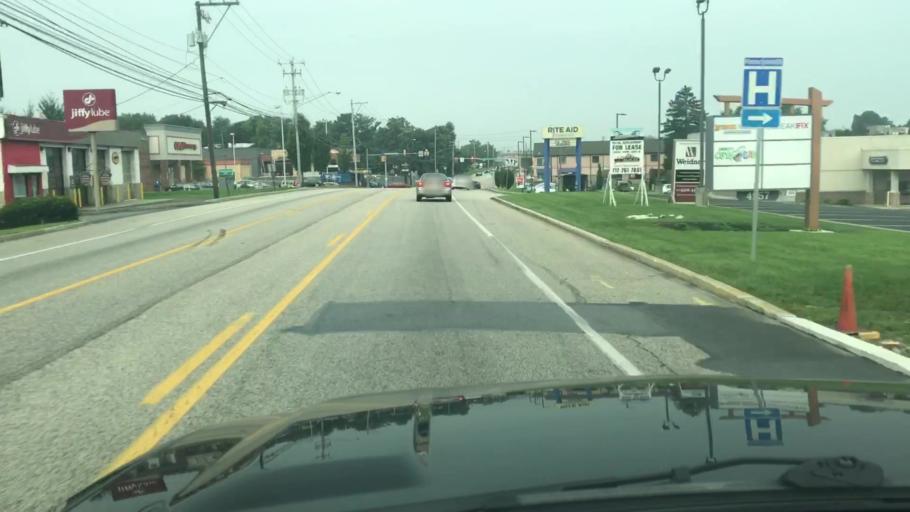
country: US
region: Pennsylvania
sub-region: Cumberland County
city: Shiremanstown
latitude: 40.2372
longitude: -76.9701
